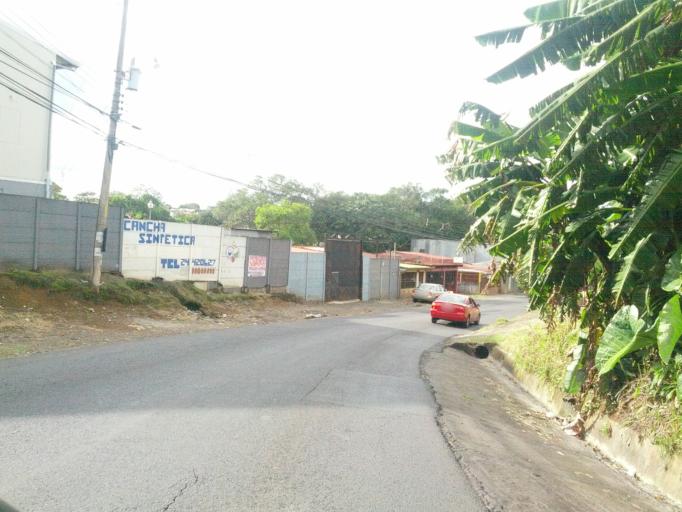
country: CR
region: Alajuela
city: Alajuela
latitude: 10.0180
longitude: -84.1967
